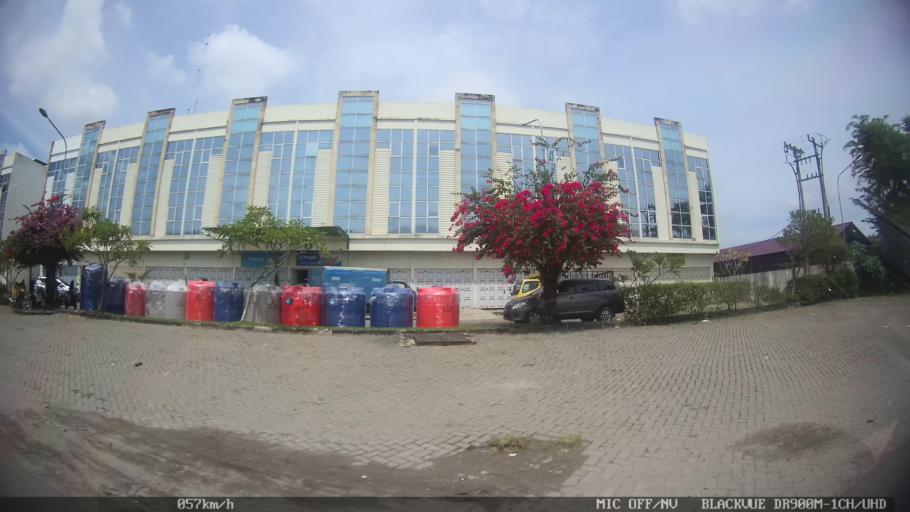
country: ID
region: North Sumatra
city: Medan
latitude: 3.6431
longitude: 98.7085
